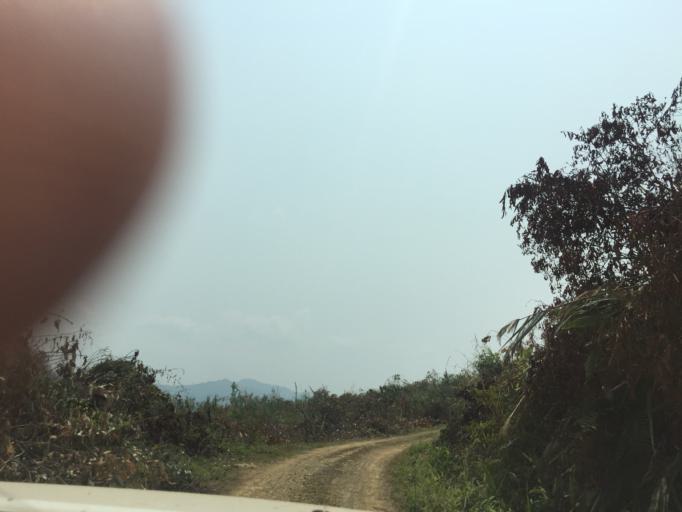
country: LA
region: Loungnamtha
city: Muang Nale
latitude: 20.6198
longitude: 101.6120
